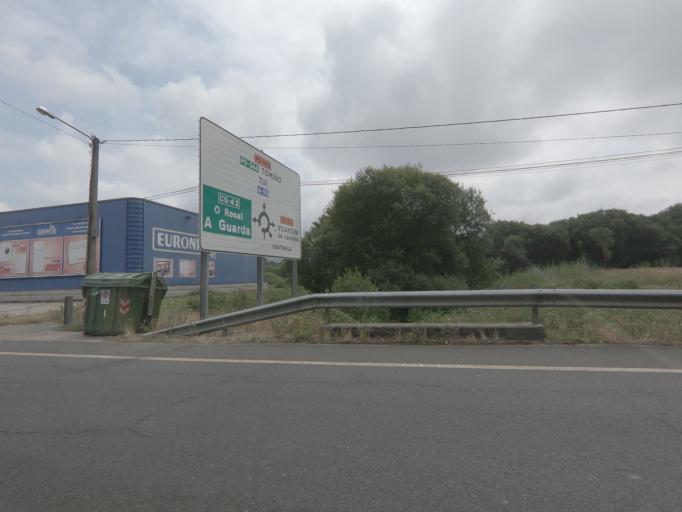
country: PT
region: Viana do Castelo
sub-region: Vila Nova de Cerveira
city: Vila Nova de Cerveira
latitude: 41.9526
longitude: -8.7680
